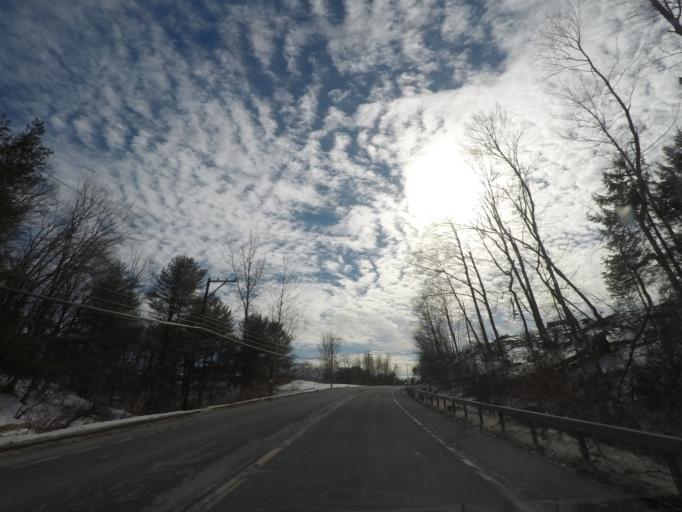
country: US
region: New York
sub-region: Albany County
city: Westmere
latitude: 42.6849
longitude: -73.9016
